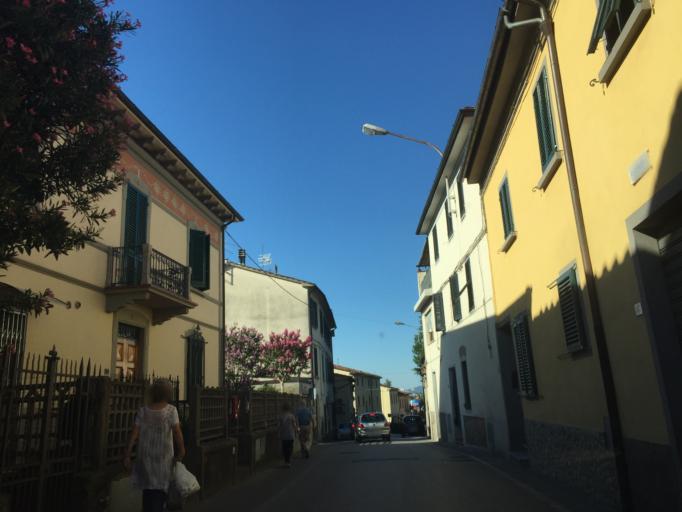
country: IT
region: Tuscany
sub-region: Provincia di Pistoia
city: Pistoia
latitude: 43.9539
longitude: 10.9418
